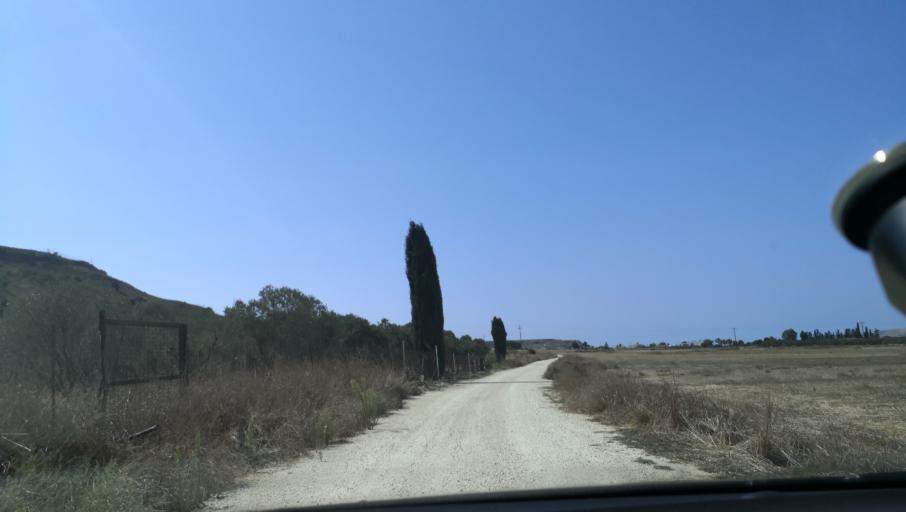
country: CY
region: Lefkosia
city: Mammari
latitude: 35.1769
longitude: 33.2161
